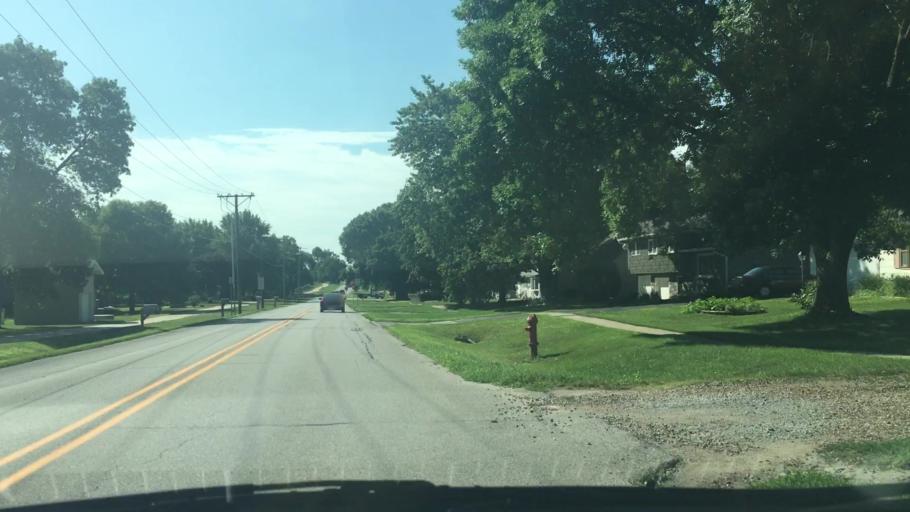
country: US
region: Iowa
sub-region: Johnson County
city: North Liberty
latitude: 41.7463
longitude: -91.5944
